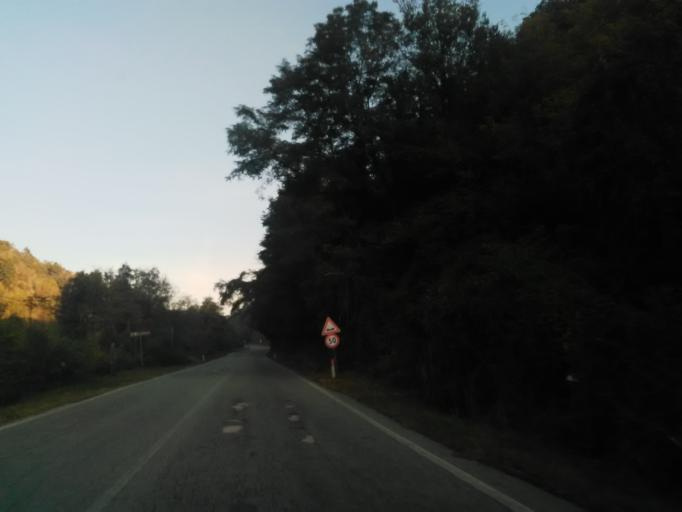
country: IT
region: Piedmont
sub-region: Provincia di Biella
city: Sostegno
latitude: 45.6606
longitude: 8.2665
